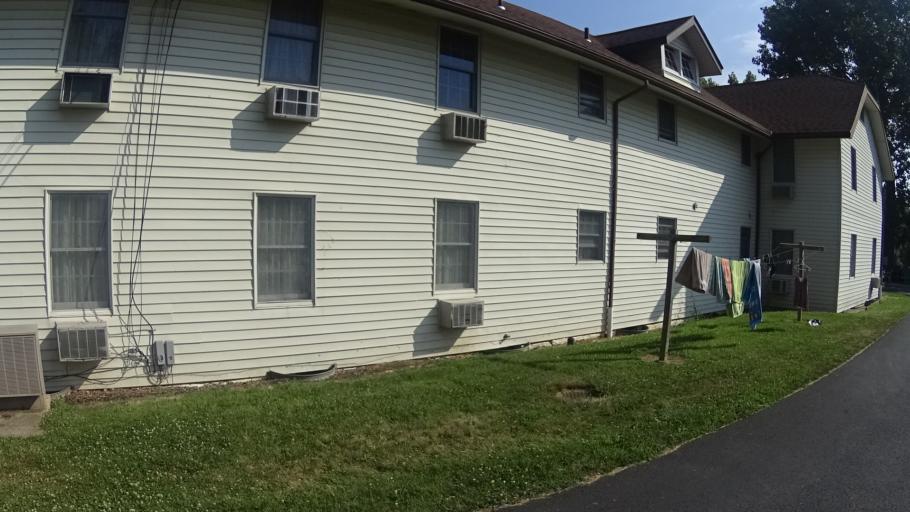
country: US
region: Ohio
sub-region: Lorain County
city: Vermilion
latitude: 41.3925
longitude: -82.4418
